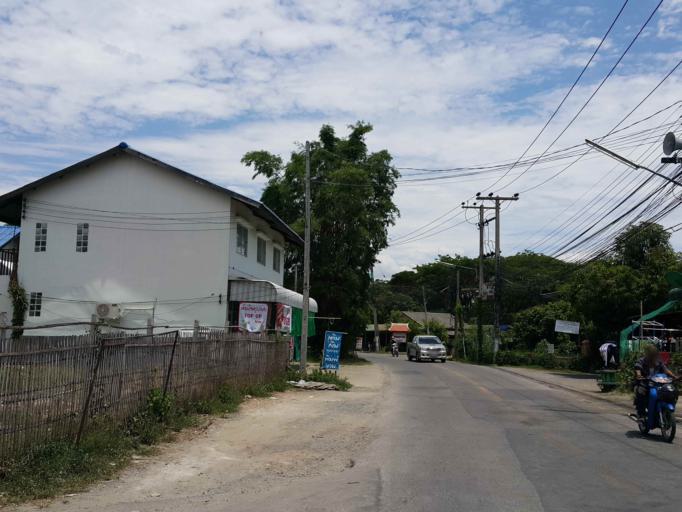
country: TH
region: Chiang Mai
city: Chiang Mai
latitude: 18.7730
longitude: 99.0215
